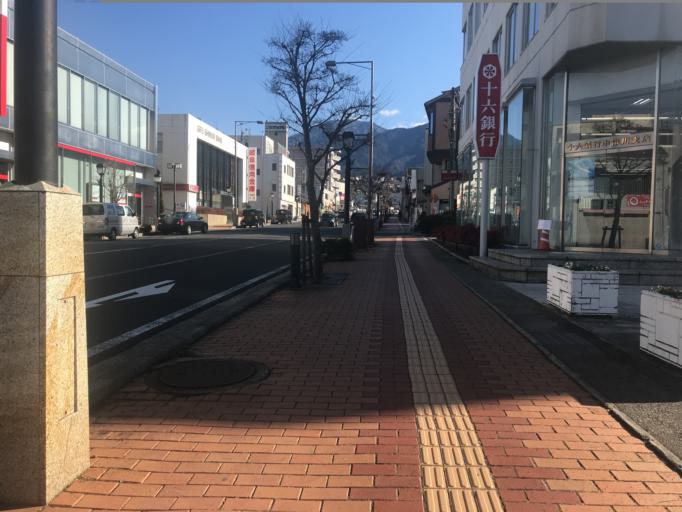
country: JP
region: Gifu
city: Nakatsugawa
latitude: 35.4992
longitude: 137.5047
